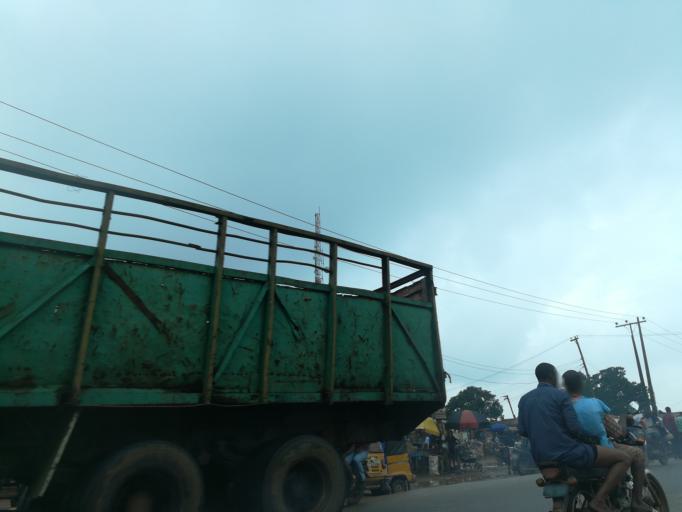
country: NG
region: Lagos
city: Ikorodu
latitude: 6.6462
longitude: 3.5174
